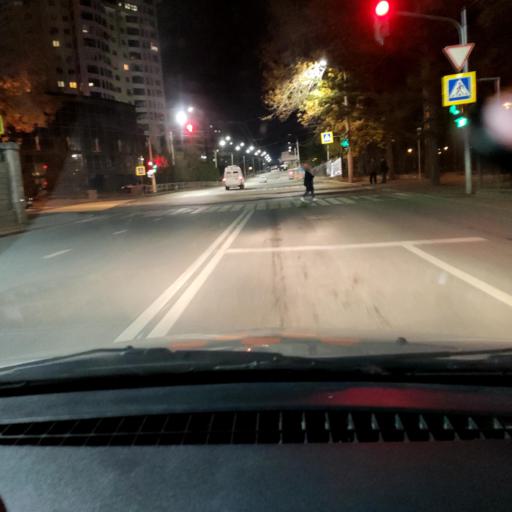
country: RU
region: Bashkortostan
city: Ufa
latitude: 54.6928
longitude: 56.0019
